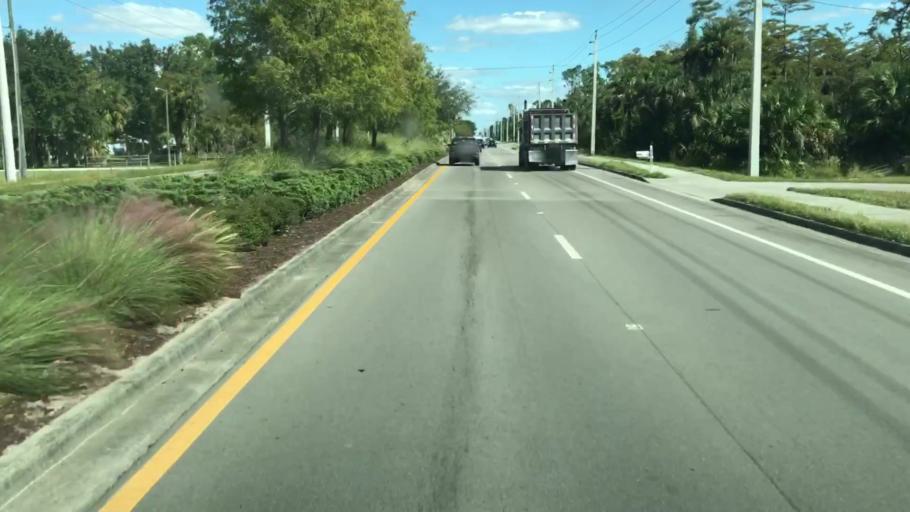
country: US
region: Florida
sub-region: Collier County
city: Vineyards
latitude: 26.2293
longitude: -81.6474
